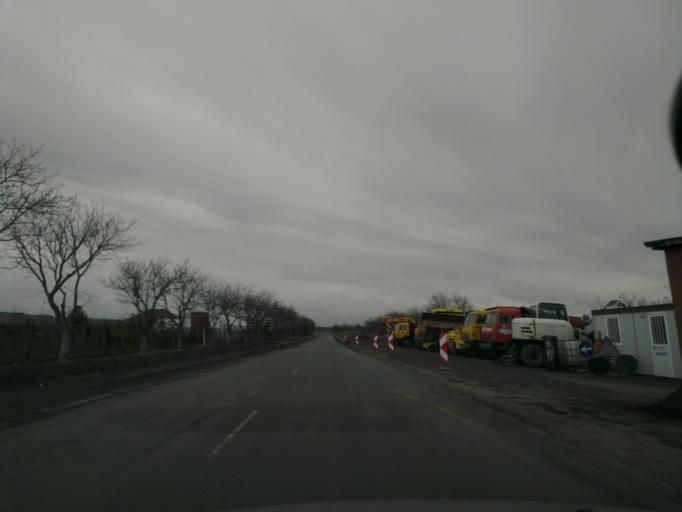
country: MD
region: Laloveni
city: Ialoveni
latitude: 46.9923
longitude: 28.7393
